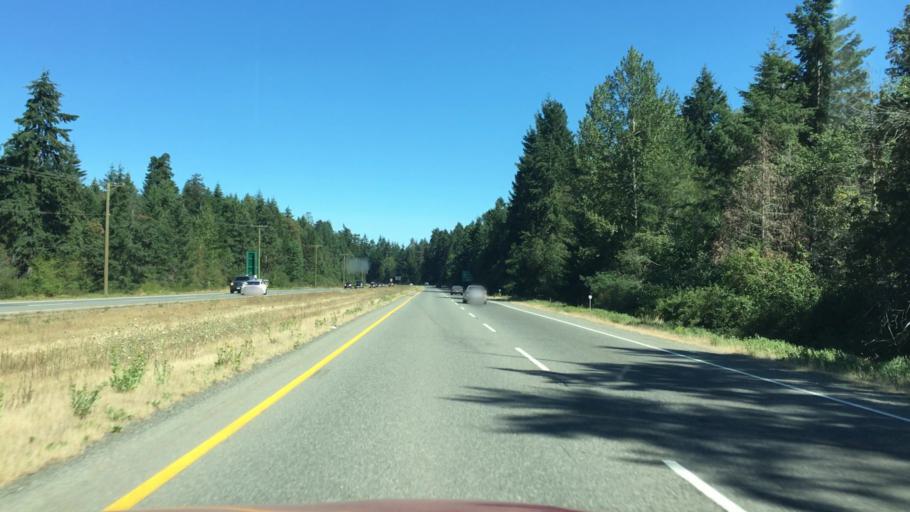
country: CA
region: British Columbia
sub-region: Regional District of Nanaimo
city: Parksville
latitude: 49.2996
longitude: -124.2885
